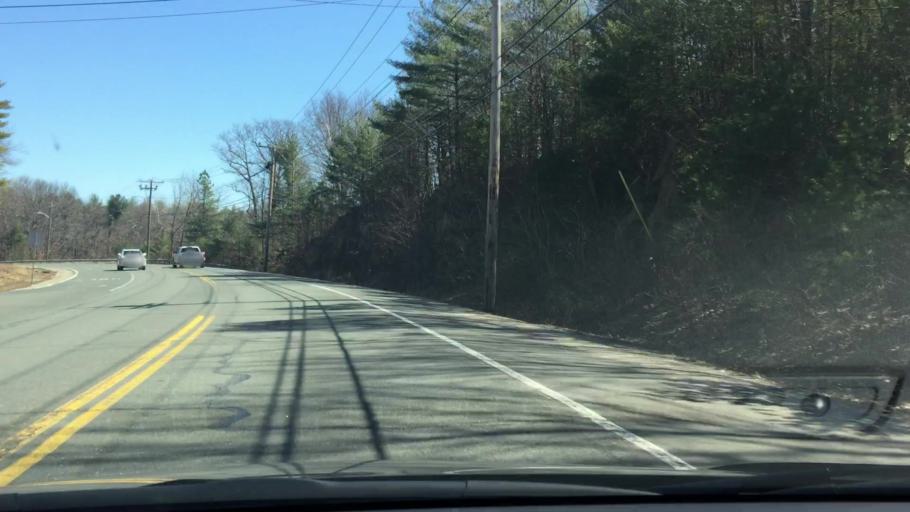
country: US
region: Massachusetts
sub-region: Hampden County
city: Holyoke
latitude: 42.1830
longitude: -72.6664
